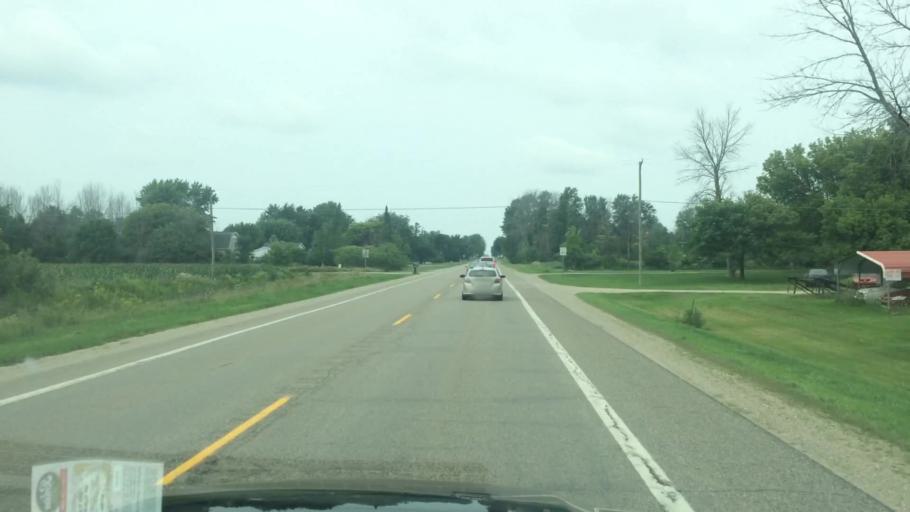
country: US
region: Michigan
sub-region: Huron County
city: Bad Axe
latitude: 43.8890
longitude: -83.0031
